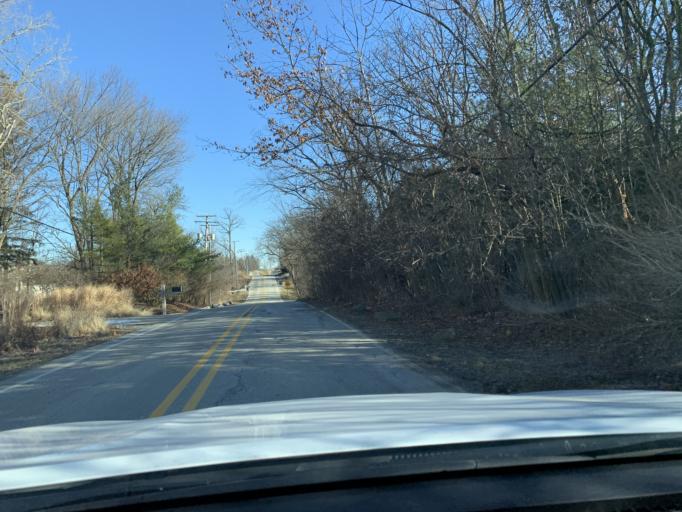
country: US
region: Illinois
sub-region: DuPage County
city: Burr Ridge
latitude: 41.7311
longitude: -87.9176
